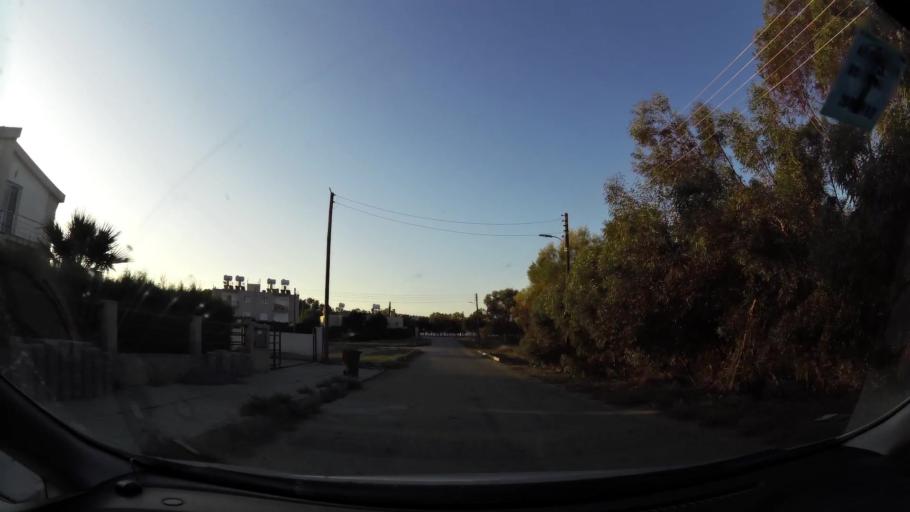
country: CY
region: Lefkosia
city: Nicosia
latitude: 35.1922
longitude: 33.3198
